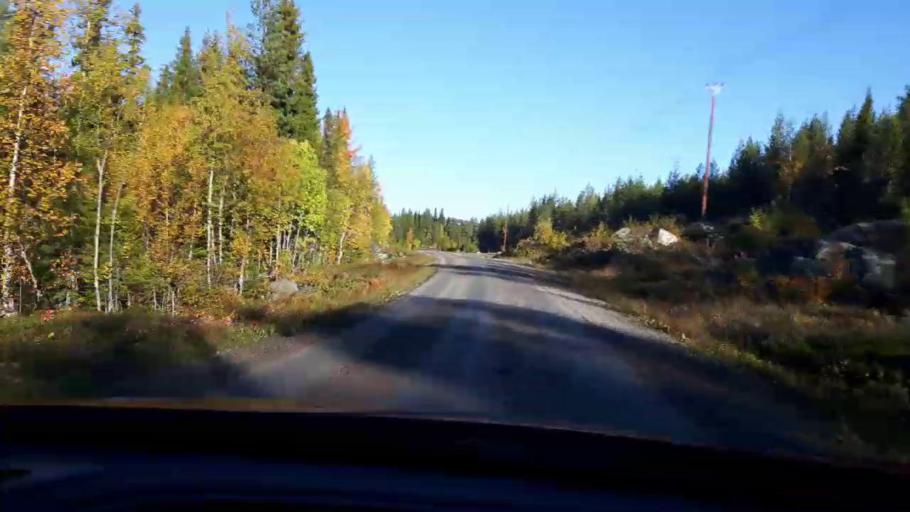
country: SE
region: Jaemtland
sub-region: Stroemsunds Kommun
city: Stroemsund
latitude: 64.3669
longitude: 15.1635
